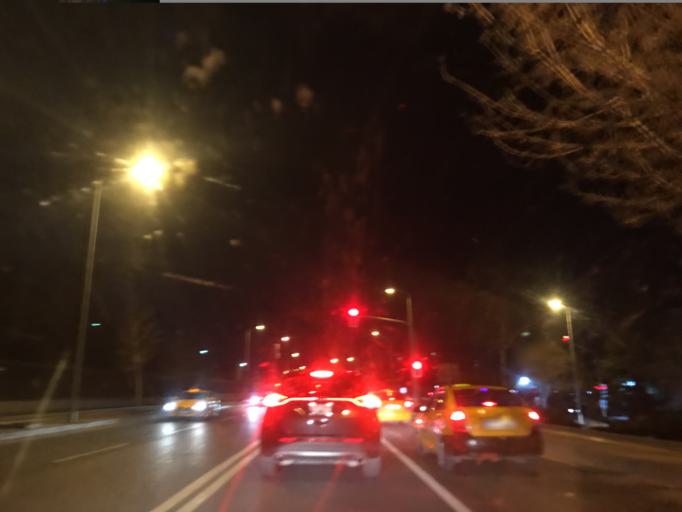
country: TR
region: Ankara
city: Cankaya
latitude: 39.8842
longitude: 32.8670
